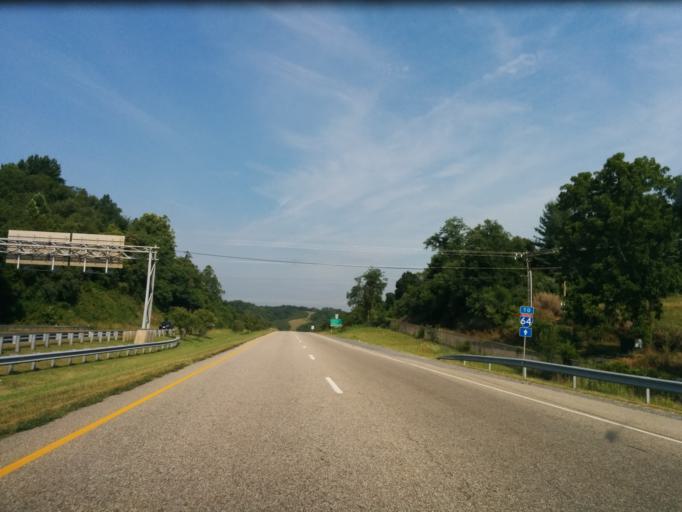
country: US
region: Virginia
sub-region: Rockbridge County
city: East Lexington
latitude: 37.7575
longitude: -79.4123
